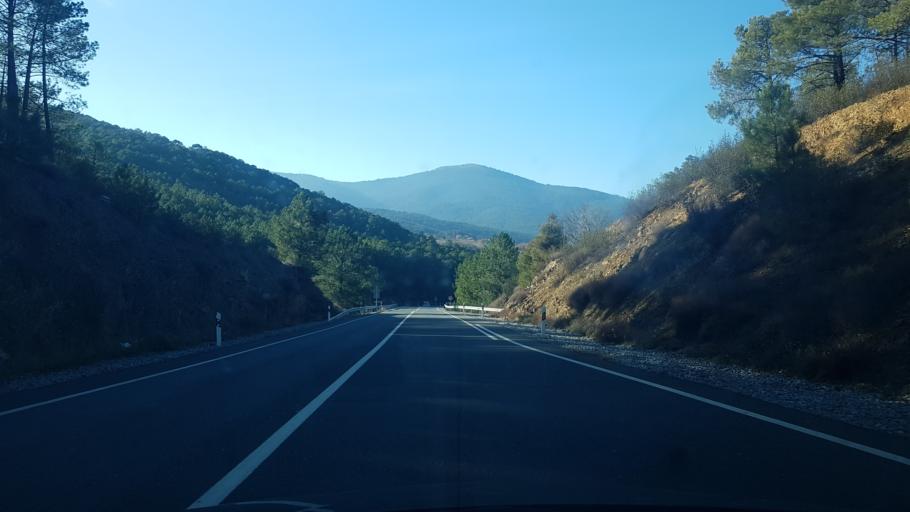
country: ES
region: Castille and Leon
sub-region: Provincia de Avila
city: El Tiemblo
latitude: 40.3896
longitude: -4.4658
